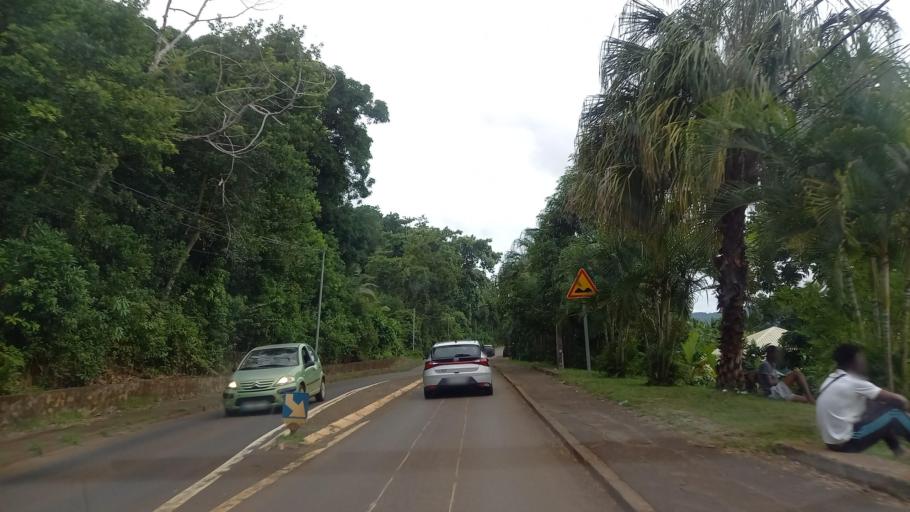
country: YT
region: Chirongui
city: Chirongui
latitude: -12.8971
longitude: 45.1440
